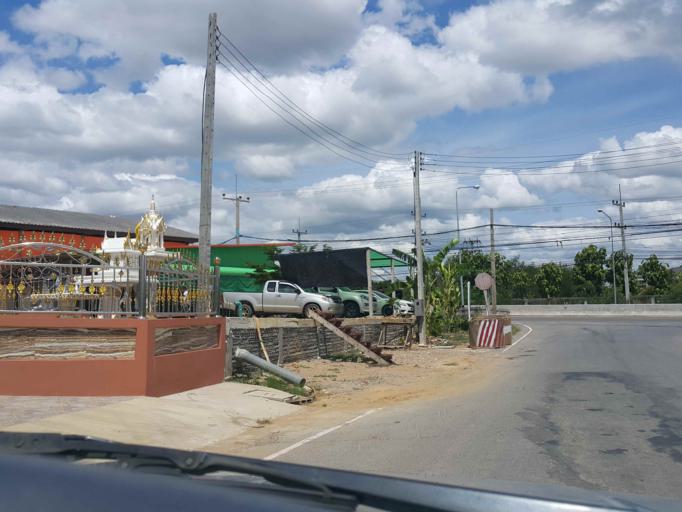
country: TH
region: Chiang Mai
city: Doi Lo
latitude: 18.4553
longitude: 98.7700
